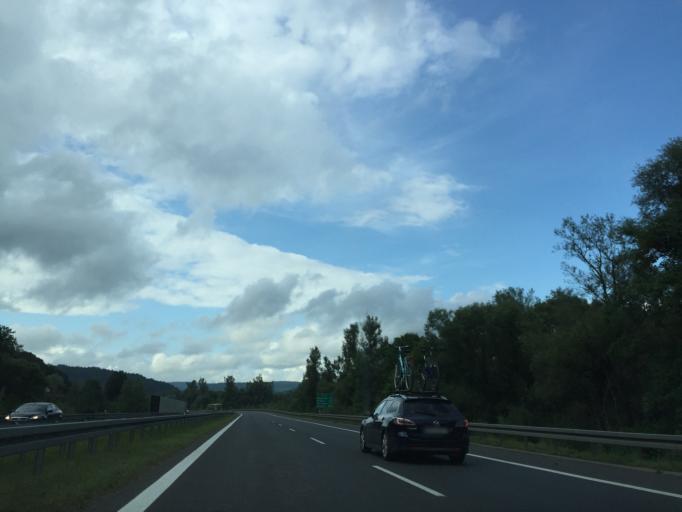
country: PL
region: Lesser Poland Voivodeship
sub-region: Powiat myslenicki
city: Lubien
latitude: 49.7238
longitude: 19.9792
